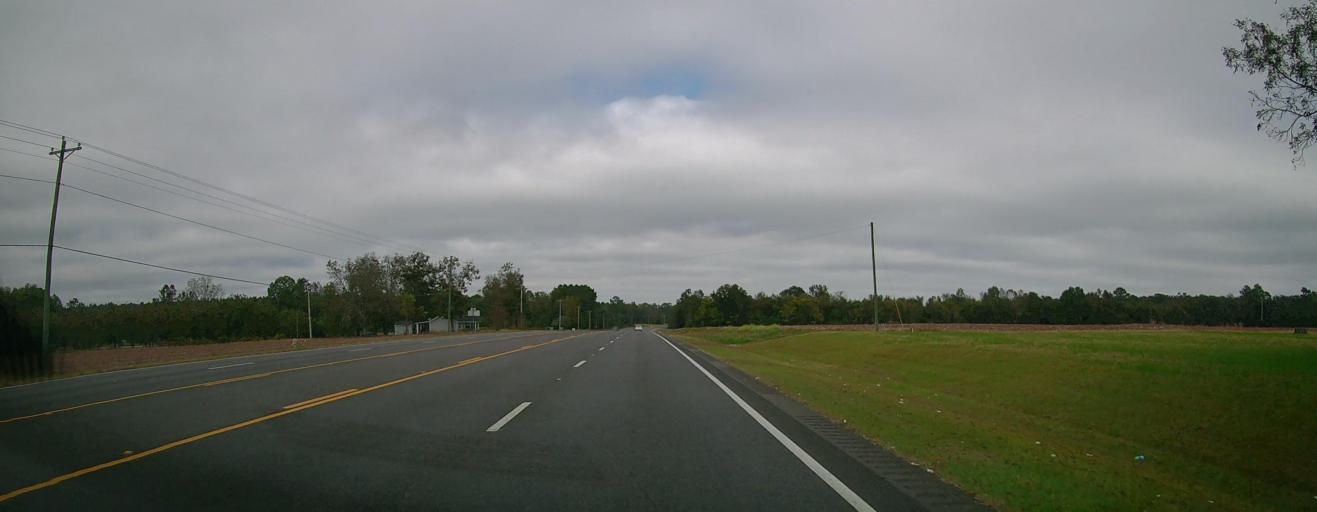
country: US
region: Georgia
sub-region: Thomas County
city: Thomasville
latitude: 30.9632
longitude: -83.8935
